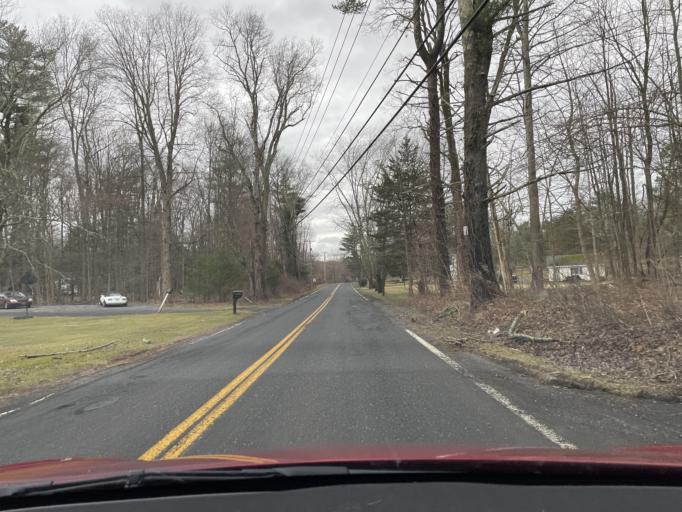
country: US
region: New York
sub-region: Ulster County
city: Manorville
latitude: 42.1070
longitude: -74.0340
